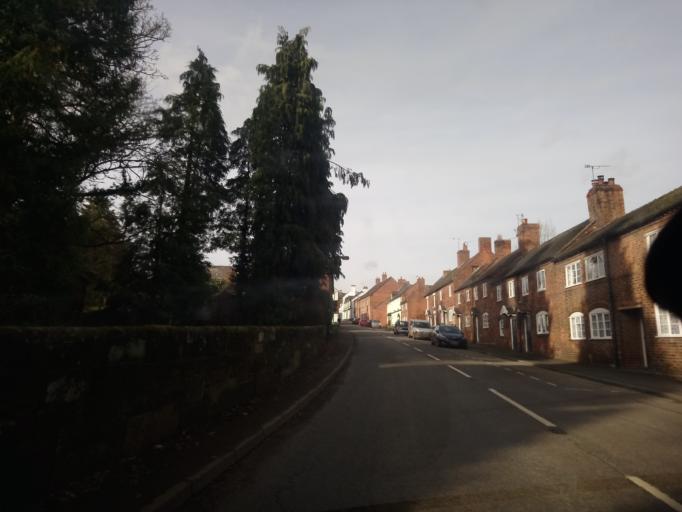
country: GB
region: England
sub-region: Shropshire
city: Stoke upon Tern
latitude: 52.8526
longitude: -2.5744
